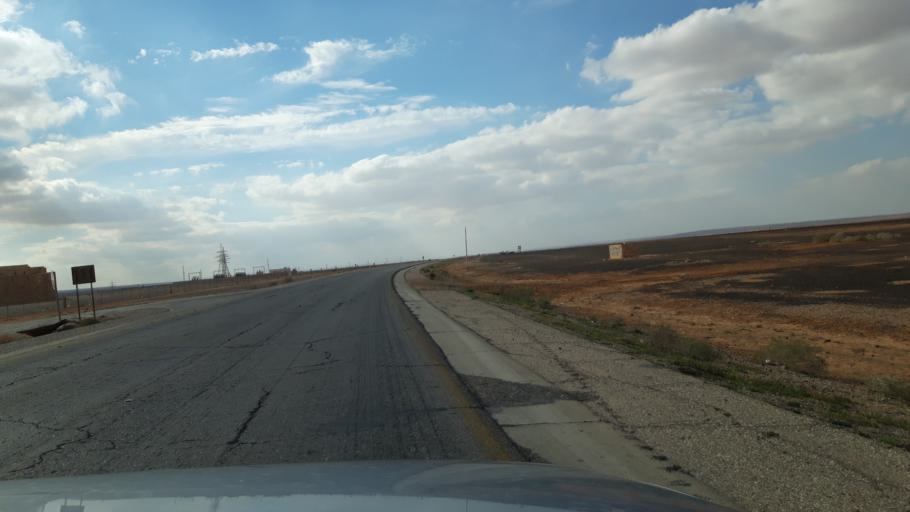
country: JO
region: Amman
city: Al Azraq ash Shamali
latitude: 31.7292
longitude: 36.4653
